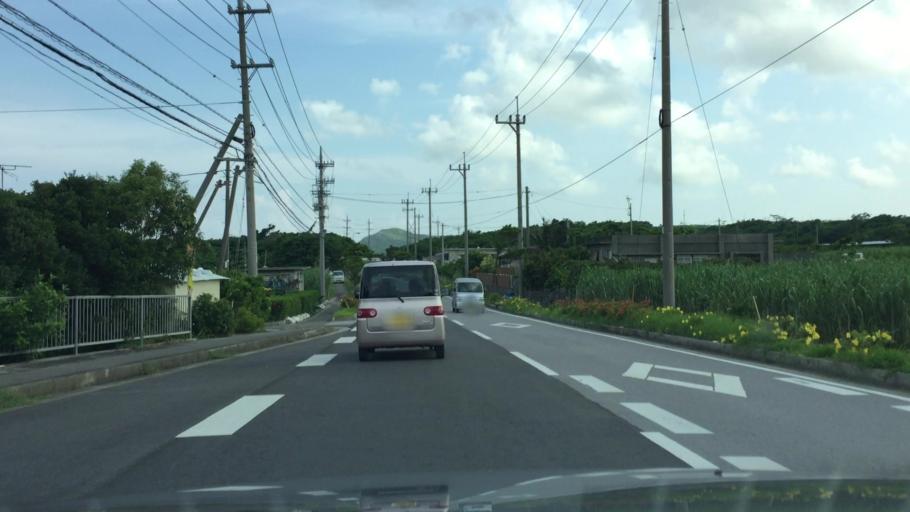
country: JP
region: Okinawa
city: Ishigaki
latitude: 24.4381
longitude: 124.2491
